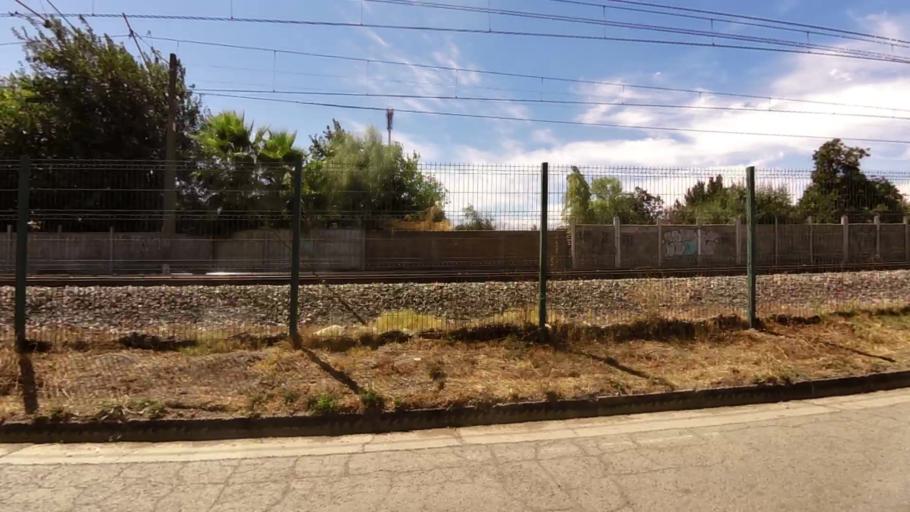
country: CL
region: O'Higgins
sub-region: Provincia de Cachapoal
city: Graneros
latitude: -33.9813
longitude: -70.7142
